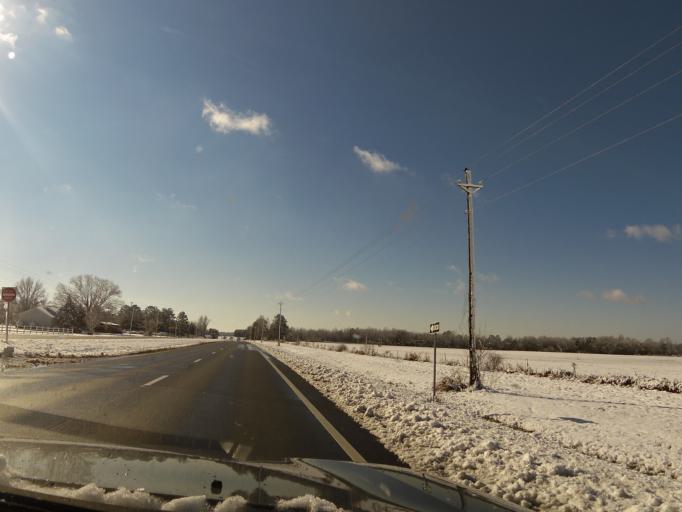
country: US
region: North Carolina
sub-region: Wilson County
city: Elm City
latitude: 35.8395
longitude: -77.8549
